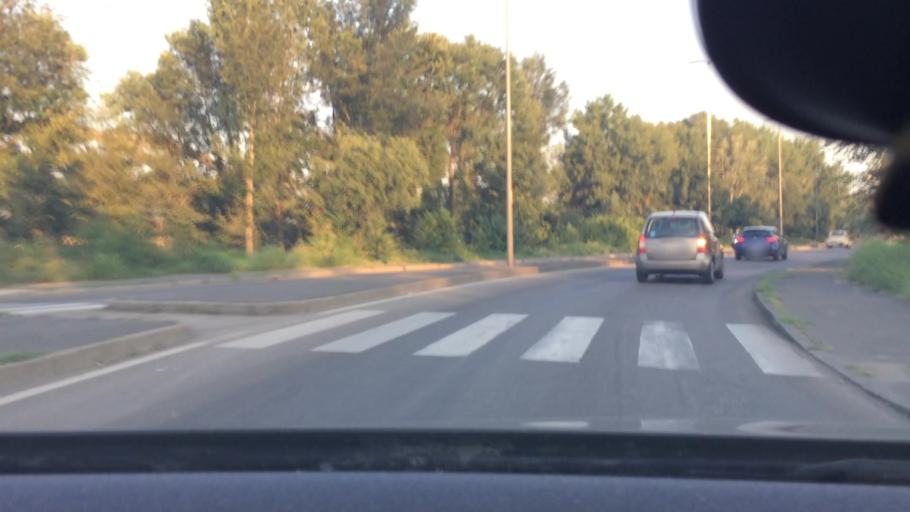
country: IT
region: Lombardy
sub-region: Citta metropolitana di Milano
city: Figino
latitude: 45.5012
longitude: 9.0734
